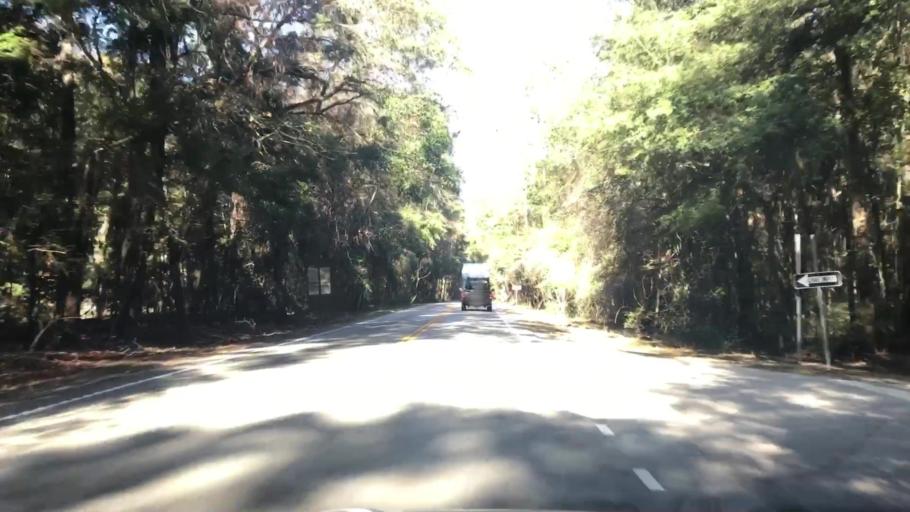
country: US
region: South Carolina
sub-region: Charleston County
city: Shell Point
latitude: 32.8653
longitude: -80.0836
